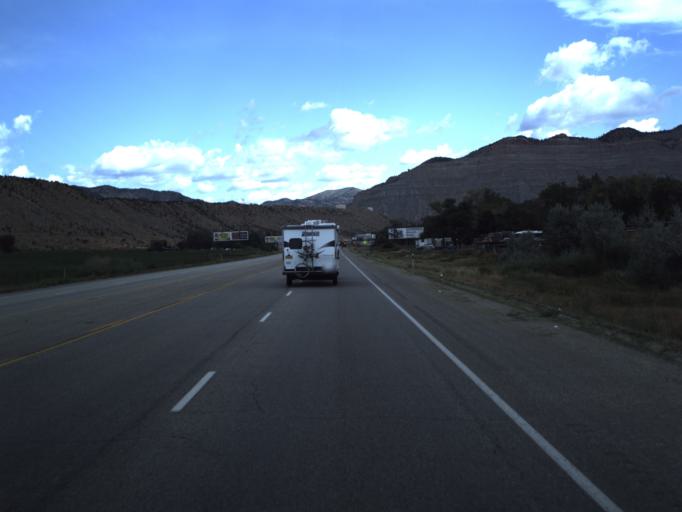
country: US
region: Utah
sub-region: Carbon County
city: Spring Glen
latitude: 39.6612
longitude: -110.8608
